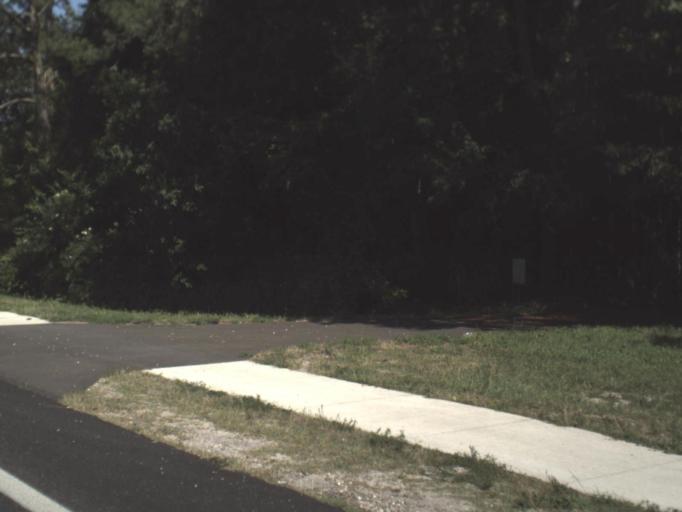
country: US
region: Florida
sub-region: Saint Johns County
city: Saint Augustine
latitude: 29.9146
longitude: -81.3817
